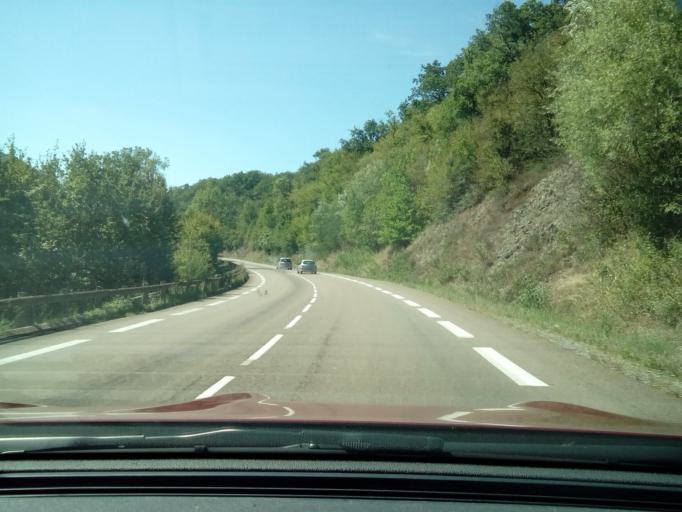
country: FR
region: Rhone-Alpes
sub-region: Departement du Rhone
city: Saint-Verand
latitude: 45.9017
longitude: 4.5564
